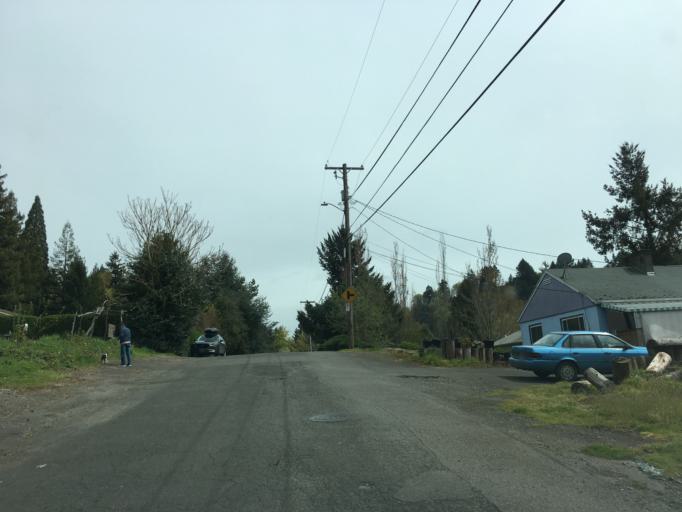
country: US
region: Oregon
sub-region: Multnomah County
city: Lents
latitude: 45.5496
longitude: -122.5744
